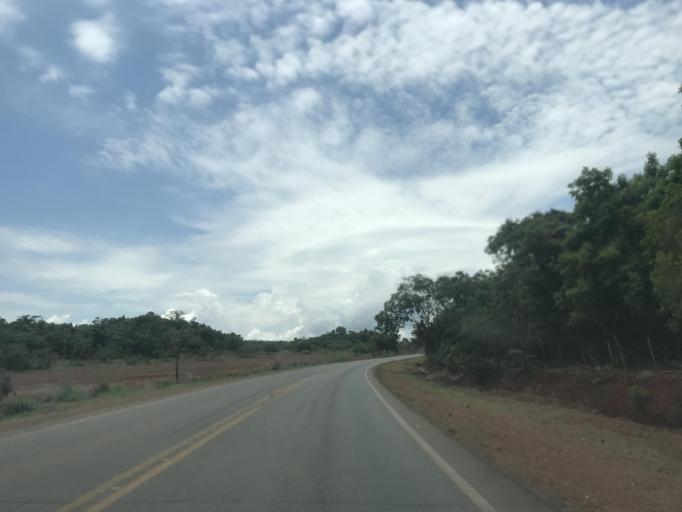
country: BR
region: Goias
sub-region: Vianopolis
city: Vianopolis
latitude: -16.7206
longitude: -48.4067
